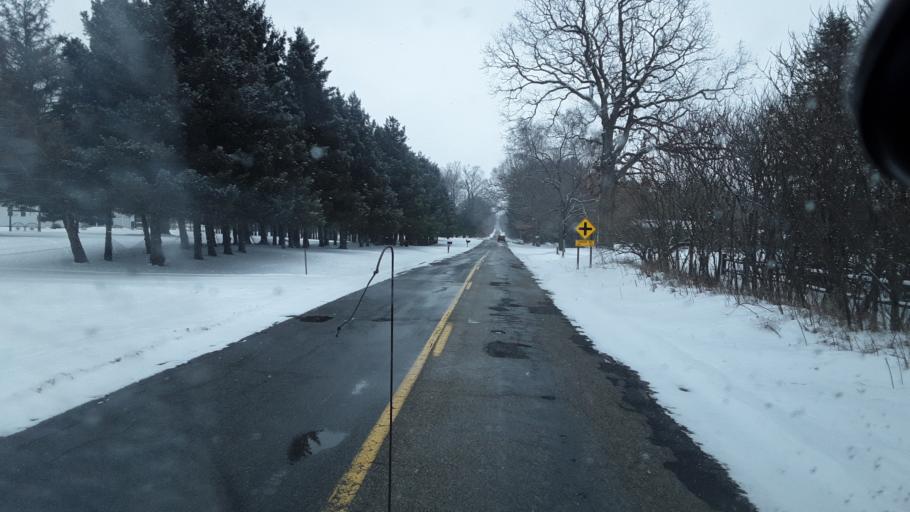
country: US
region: Michigan
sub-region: Ingham County
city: Leslie
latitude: 42.4821
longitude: -84.3942
